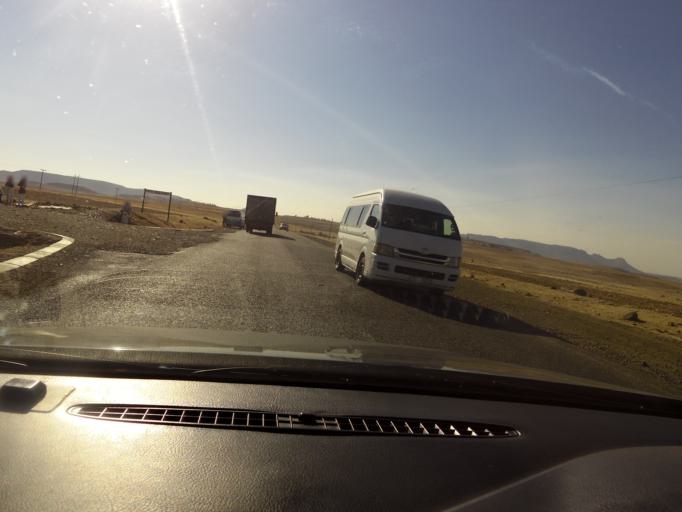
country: LS
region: Mohale's Hoek District
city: Mohale's Hoek
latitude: -30.0100
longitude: 27.3522
